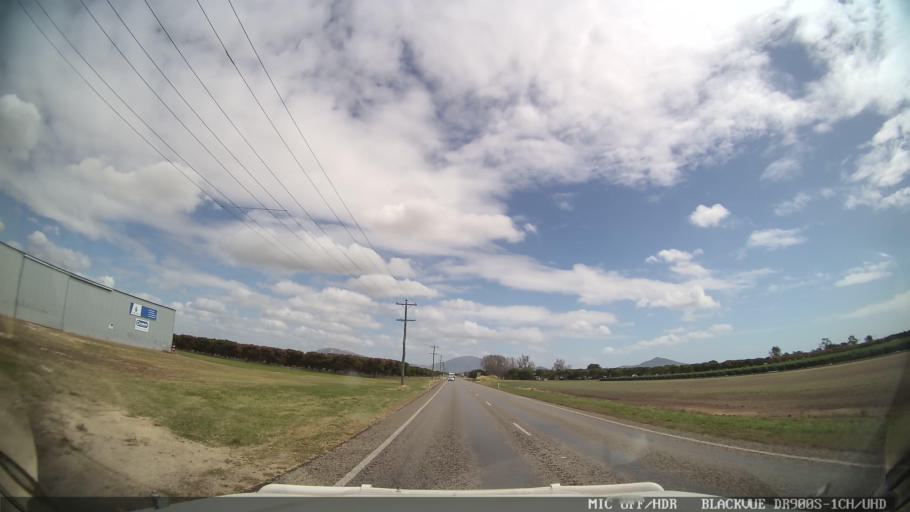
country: AU
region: Queensland
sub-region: Whitsunday
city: Bowen
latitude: -20.0156
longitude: 148.1843
